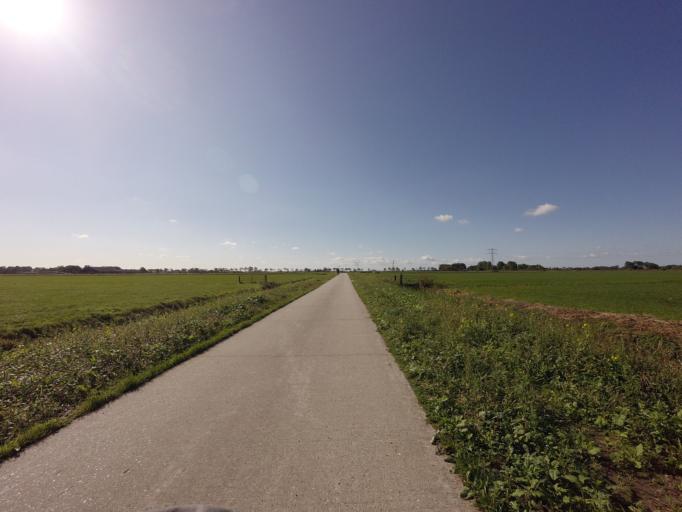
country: NL
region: Friesland
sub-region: Gemeente Leeuwarden
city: Wirdum
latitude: 53.1548
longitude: 5.7710
